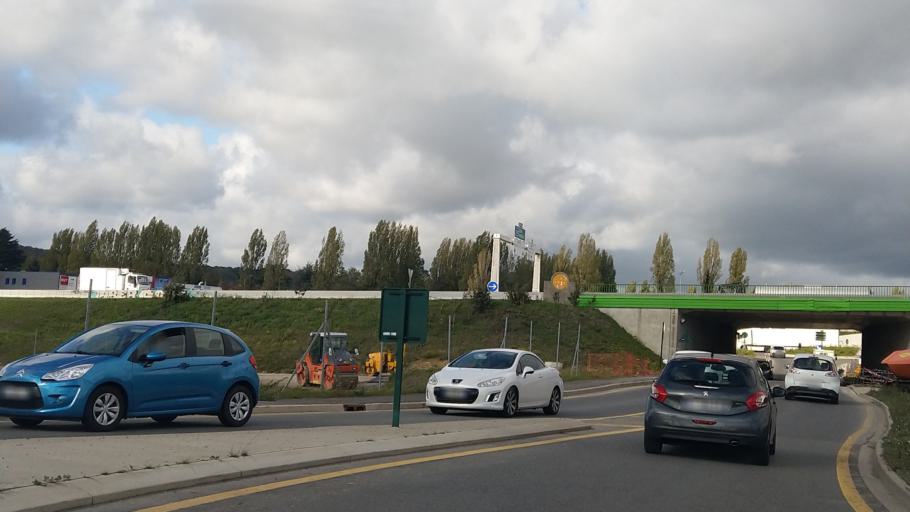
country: FR
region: Ile-de-France
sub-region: Departement du Val-d'Oise
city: Montsoult
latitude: 49.0620
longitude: 2.3279
